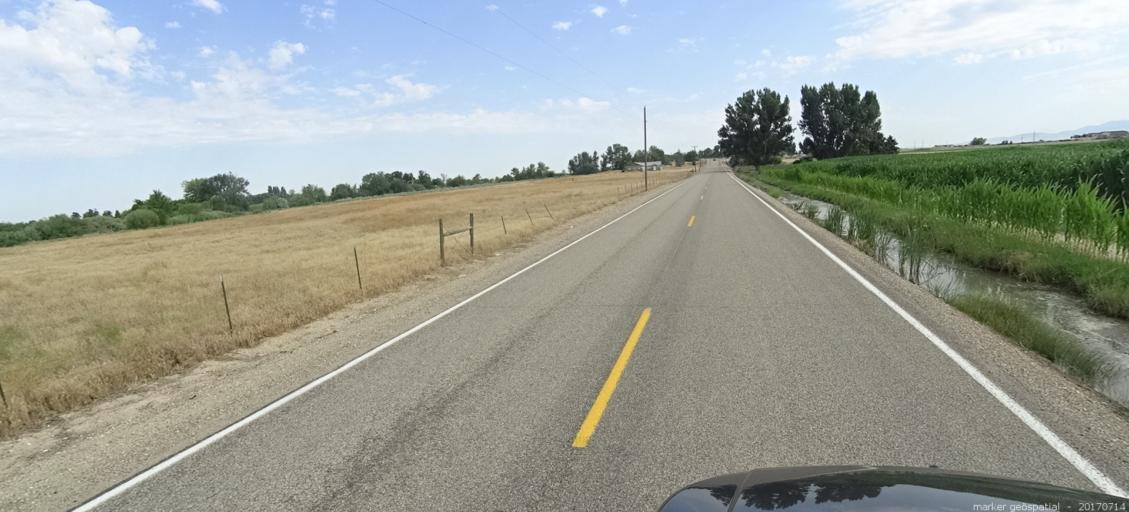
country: US
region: Idaho
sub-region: Ada County
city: Kuna
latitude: 43.4809
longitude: -116.3544
